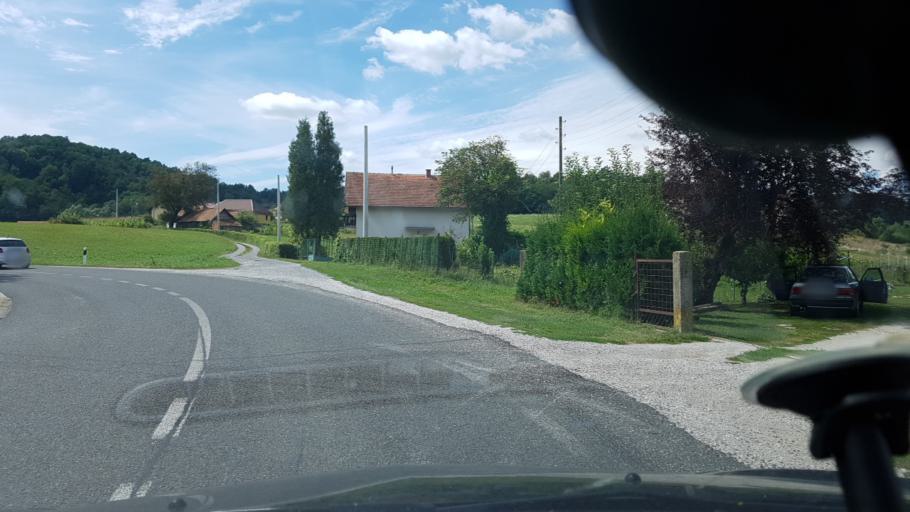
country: HR
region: Varazdinska
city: Lepoglava
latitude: 46.2203
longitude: 15.9689
